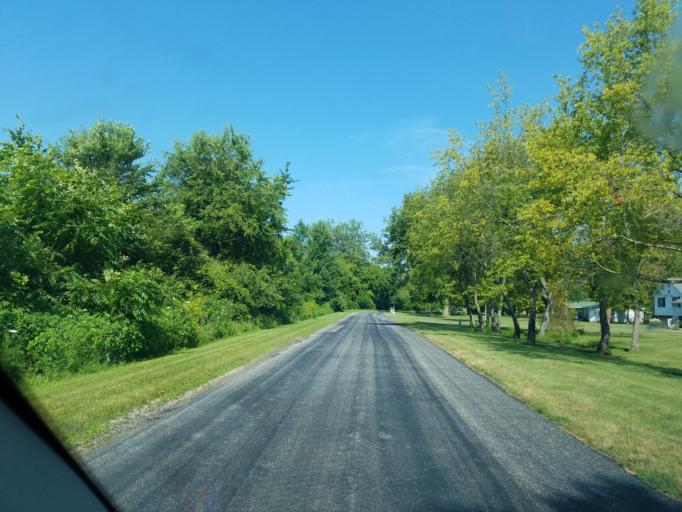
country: US
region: Ohio
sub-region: Marion County
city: Marion
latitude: 40.6453
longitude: -83.0871
